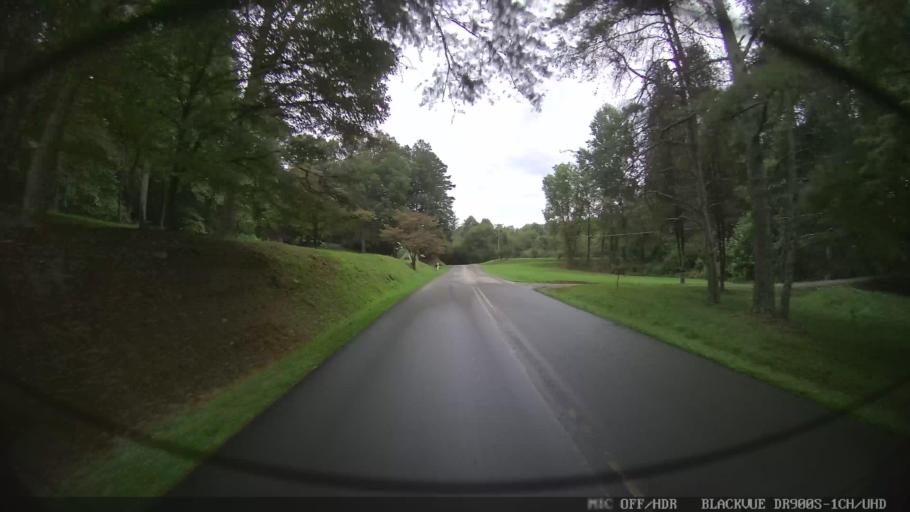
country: US
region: Georgia
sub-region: Gilmer County
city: Ellijay
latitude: 34.7557
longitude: -84.5286
